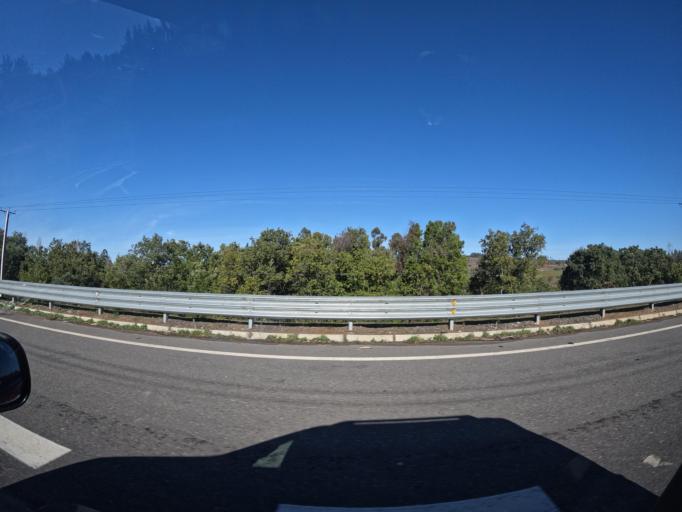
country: CL
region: Biobio
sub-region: Provincia de Biobio
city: Yumbel
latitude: -36.9992
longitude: -72.5735
